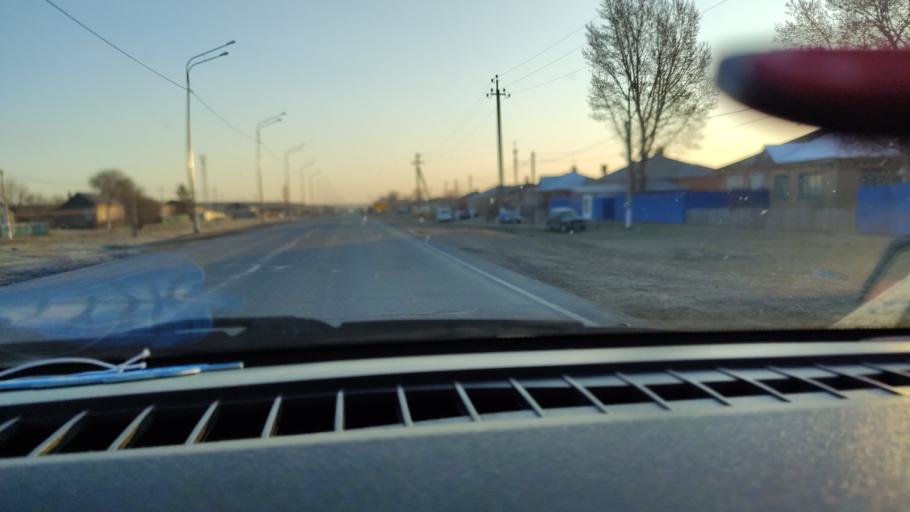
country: RU
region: Saratov
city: Sinodskoye
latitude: 51.9935
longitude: 46.6710
